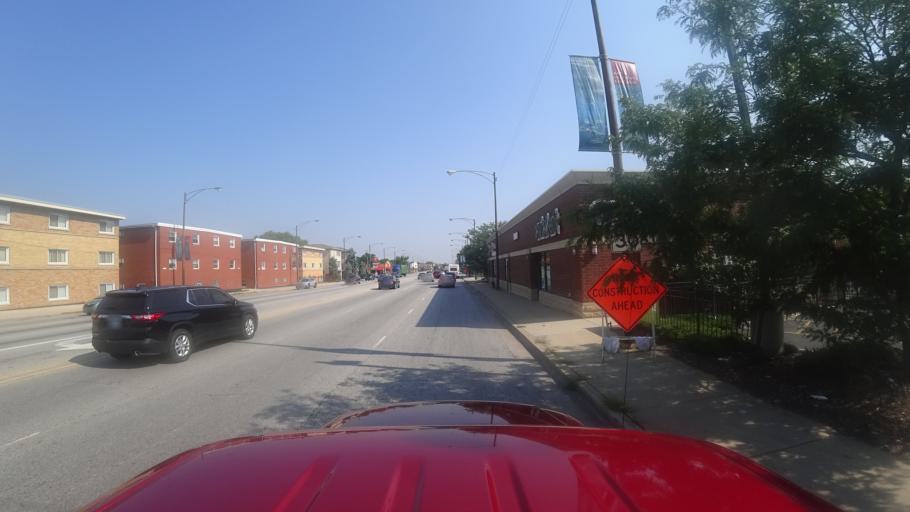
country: US
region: Illinois
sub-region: Cook County
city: Stickney
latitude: 41.7992
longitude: -87.7428
